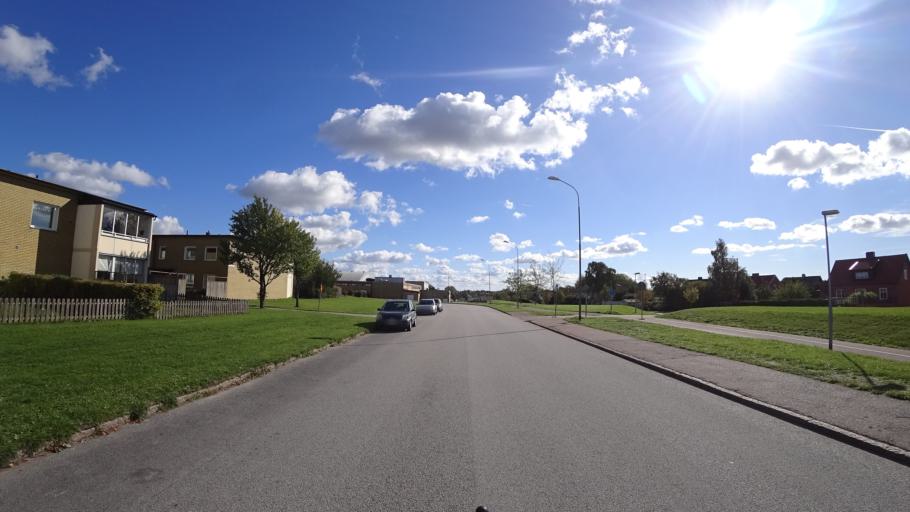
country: SE
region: Skane
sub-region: Kavlinge Kommun
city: Kaevlinge
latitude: 55.7946
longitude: 13.1004
